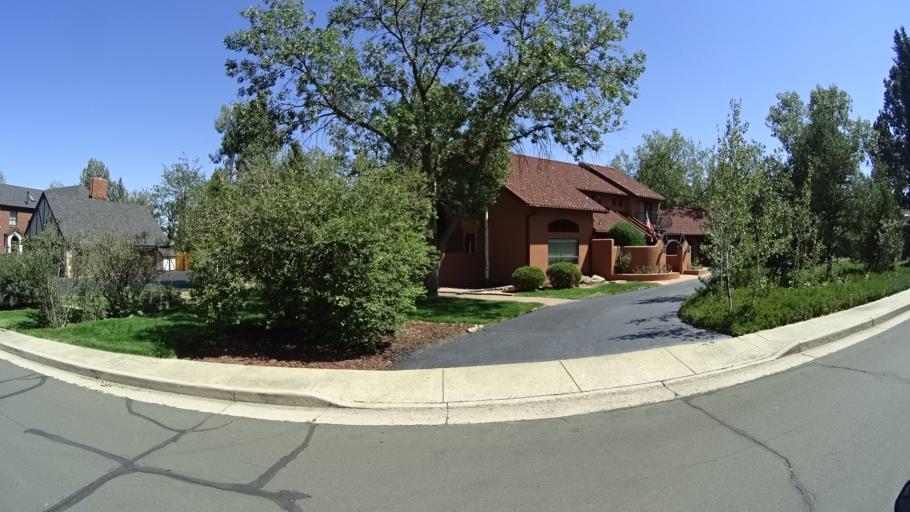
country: US
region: Colorado
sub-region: El Paso County
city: Colorado Springs
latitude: 38.7877
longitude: -104.8362
